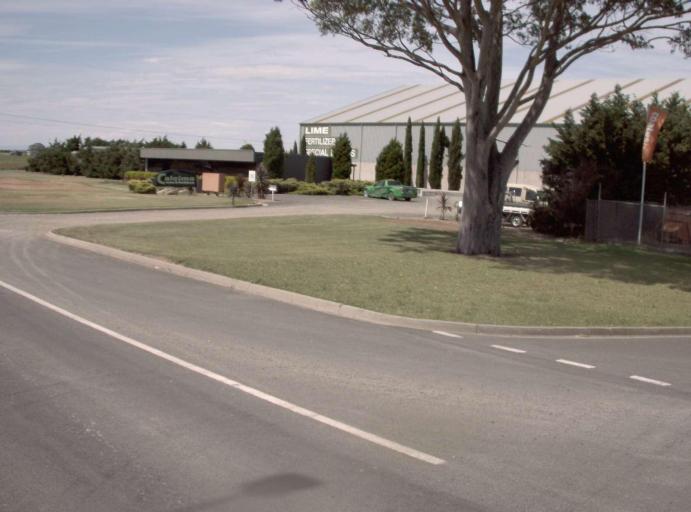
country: AU
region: Victoria
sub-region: Wellington
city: Sale
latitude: -38.0872
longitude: 147.0701
